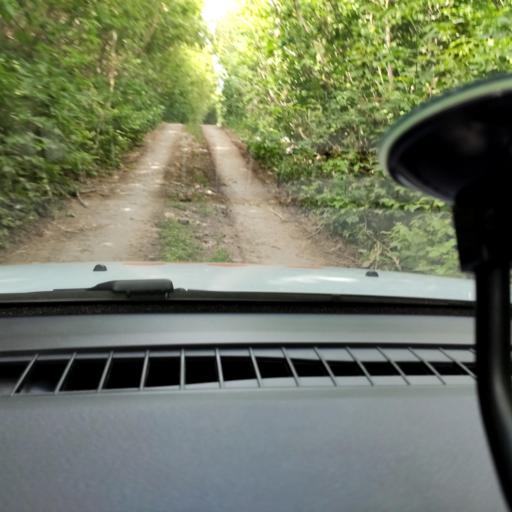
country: RU
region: Samara
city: Samara
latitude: 53.1803
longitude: 50.2186
